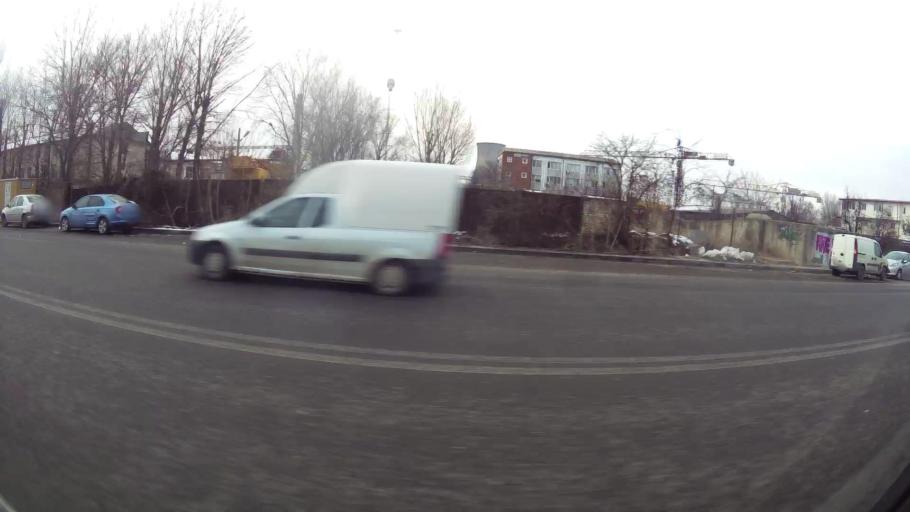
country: RO
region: Ilfov
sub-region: Comuna Popesti-Leordeni
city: Popesti-Leordeni
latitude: 44.4051
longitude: 26.1628
